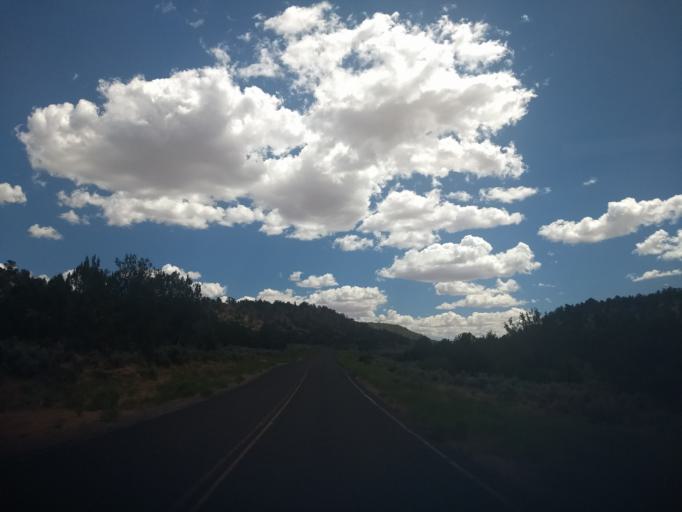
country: US
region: Utah
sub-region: Kane County
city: Kanab
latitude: 37.1146
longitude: -112.6776
